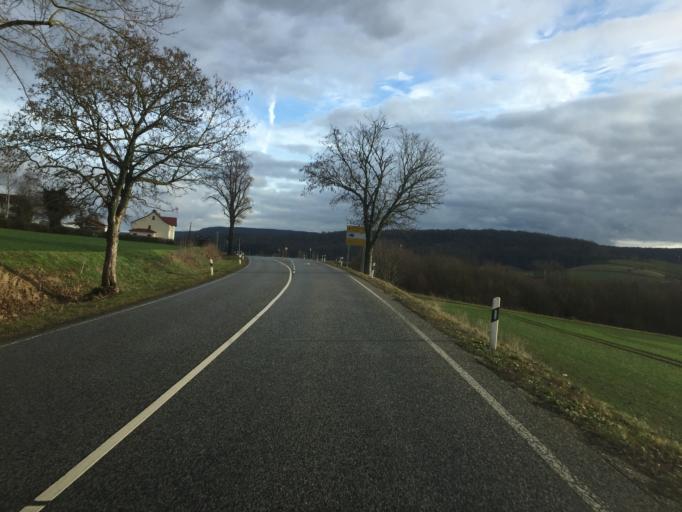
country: DE
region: Thuringia
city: Gerterode
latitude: 51.4078
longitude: 10.4737
